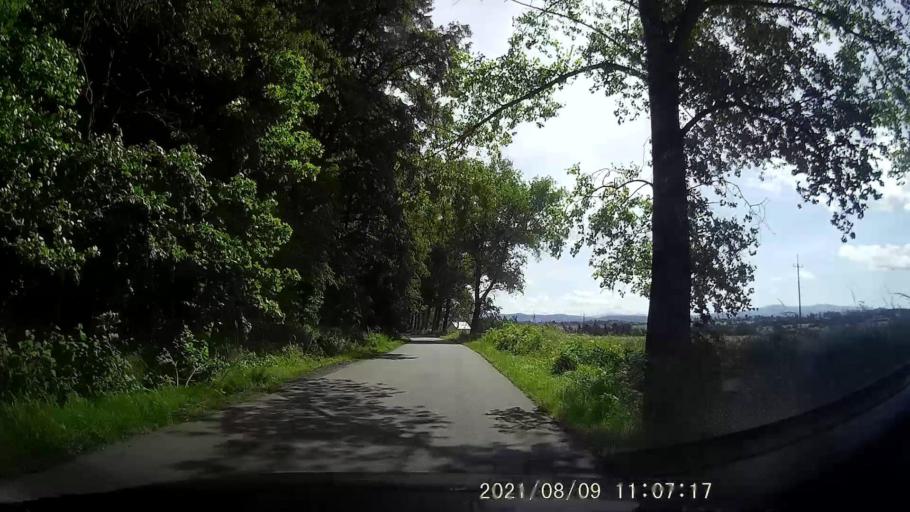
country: PL
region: Lower Silesian Voivodeship
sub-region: Powiat klodzki
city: Bozkow
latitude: 50.4562
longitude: 16.5969
